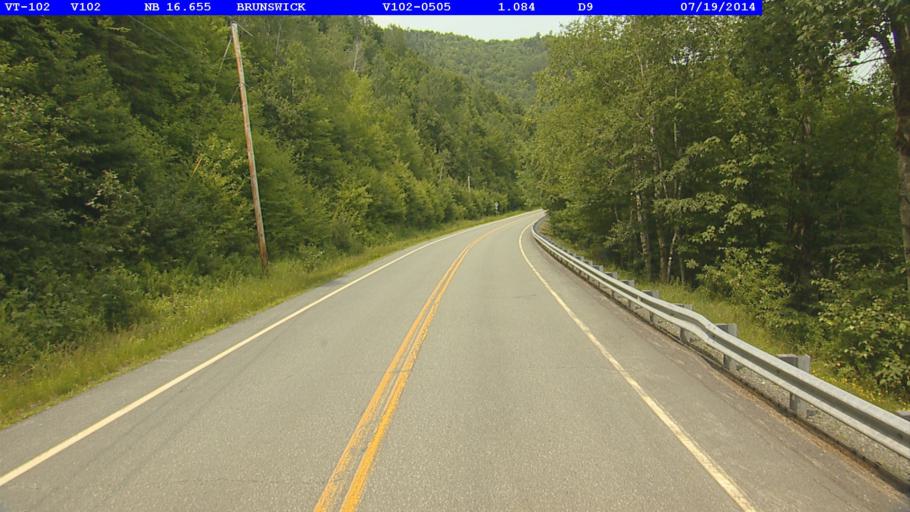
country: US
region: New Hampshire
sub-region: Coos County
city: Stratford
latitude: 44.6766
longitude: -71.5950
